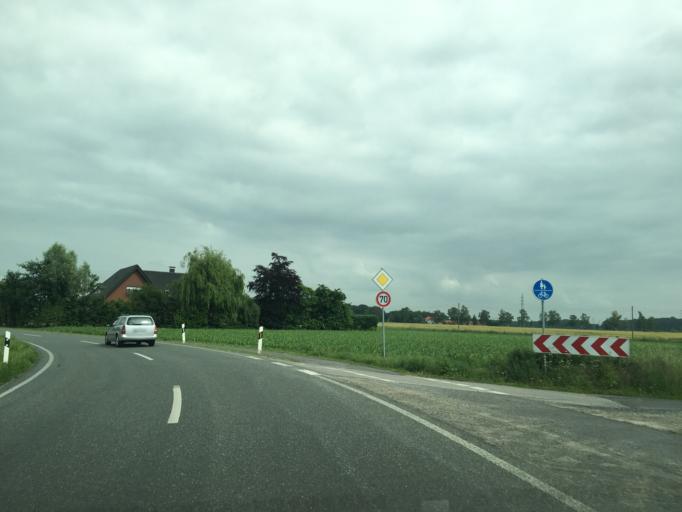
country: DE
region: North Rhine-Westphalia
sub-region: Regierungsbezirk Munster
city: Horstmar
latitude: 52.1062
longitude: 7.3042
